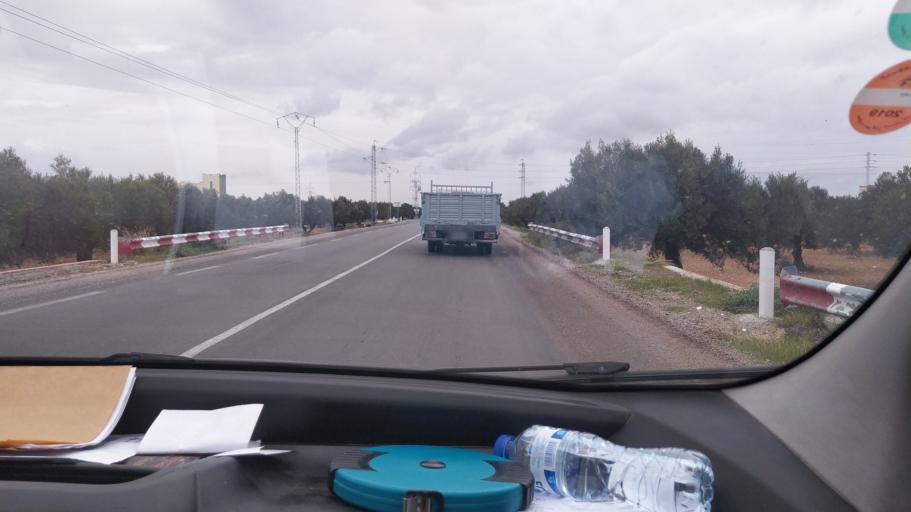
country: TN
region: Al Munastir
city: Sidi Bin Nur
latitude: 35.4840
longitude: 10.9438
